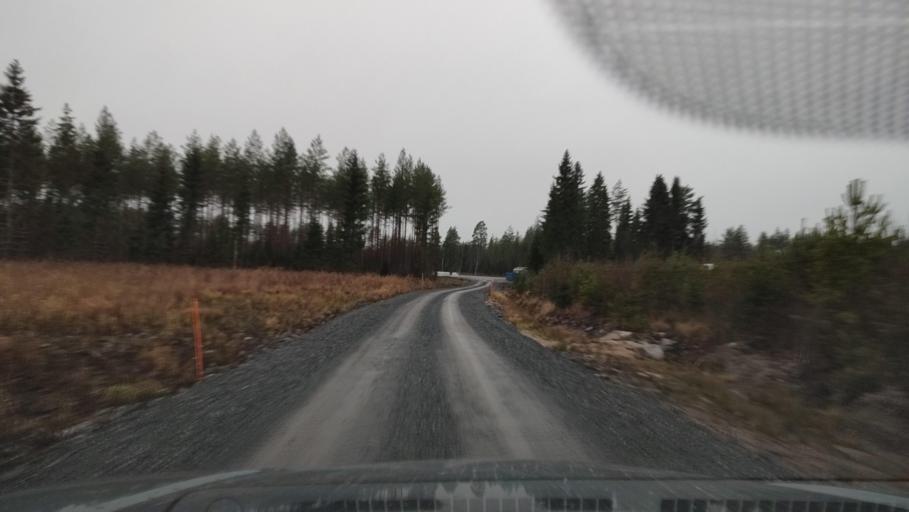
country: FI
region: Southern Ostrobothnia
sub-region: Suupohja
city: Karijoki
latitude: 62.1804
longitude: 21.5931
